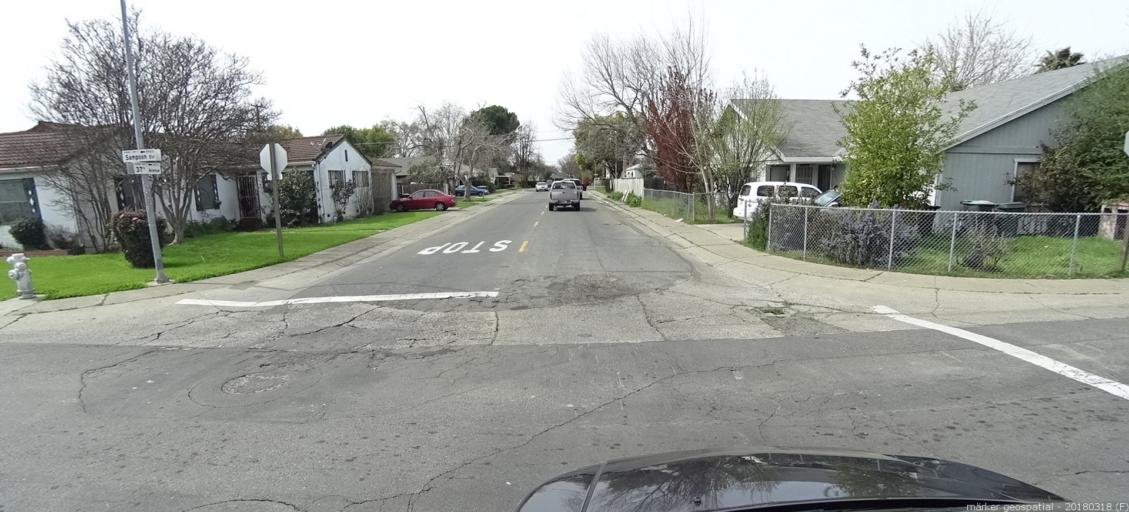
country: US
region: California
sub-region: Sacramento County
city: Parkway
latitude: 38.5197
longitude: -121.4490
